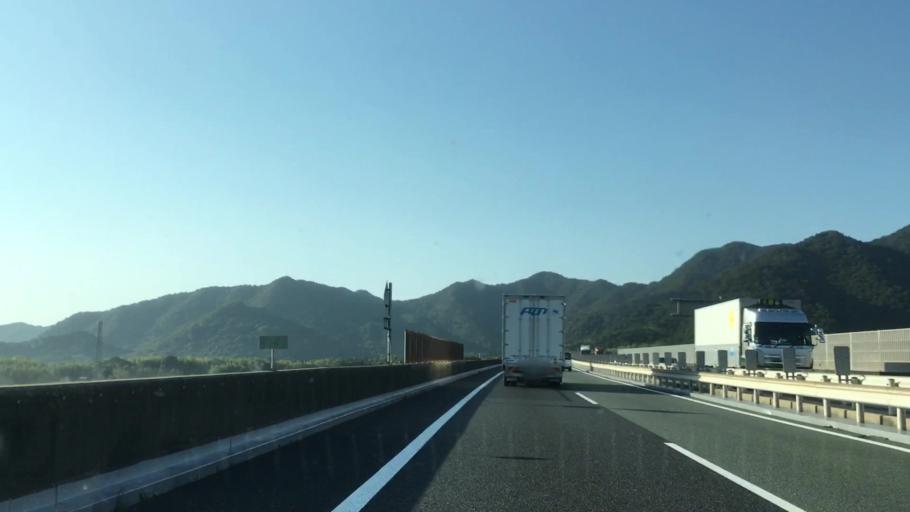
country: JP
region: Yamaguchi
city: Ogori-shimogo
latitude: 34.0924
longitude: 131.4567
